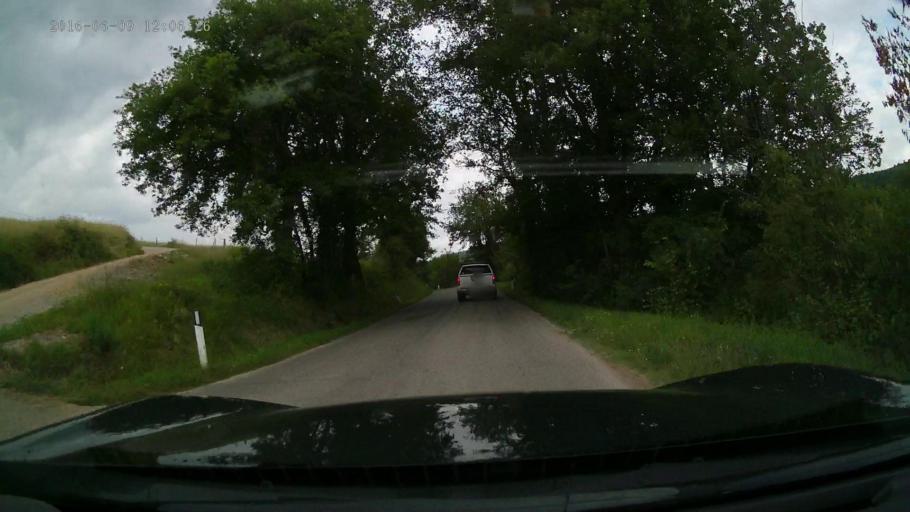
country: IT
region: Tuscany
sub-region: Province of Florence
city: Panzano in Chianti
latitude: 43.5240
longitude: 11.2906
